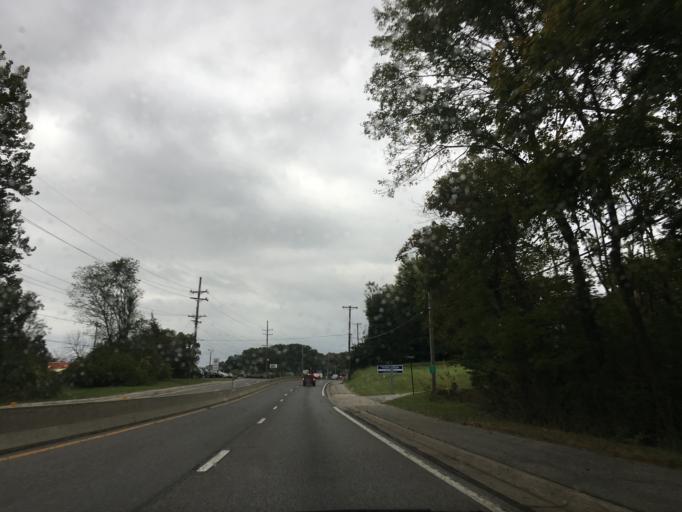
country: US
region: Missouri
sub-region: Saint Louis County
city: Maryland Heights
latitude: 38.7202
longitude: -90.4077
